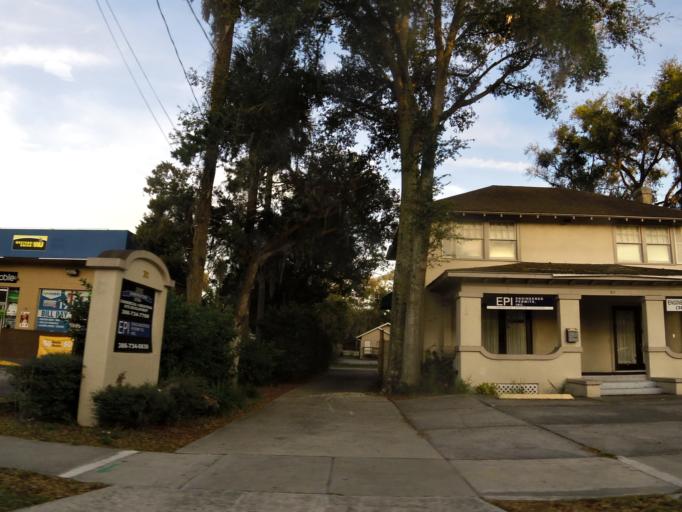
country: US
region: Florida
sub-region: Volusia County
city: DeLand
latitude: 29.0241
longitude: -81.3032
